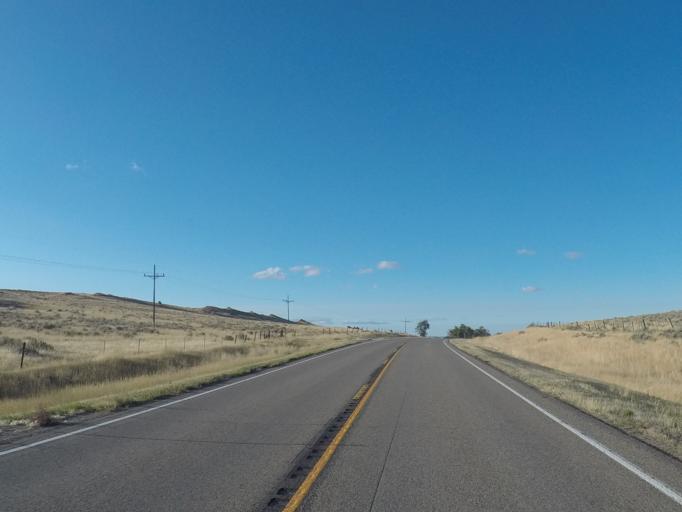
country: US
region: Montana
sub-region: Golden Valley County
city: Ryegate
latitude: 46.2397
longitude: -108.9356
